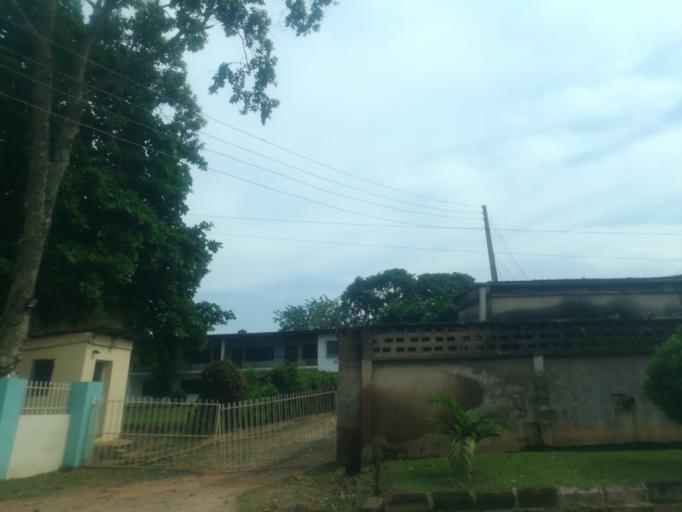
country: NG
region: Oyo
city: Ibadan
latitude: 7.4224
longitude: 3.9052
